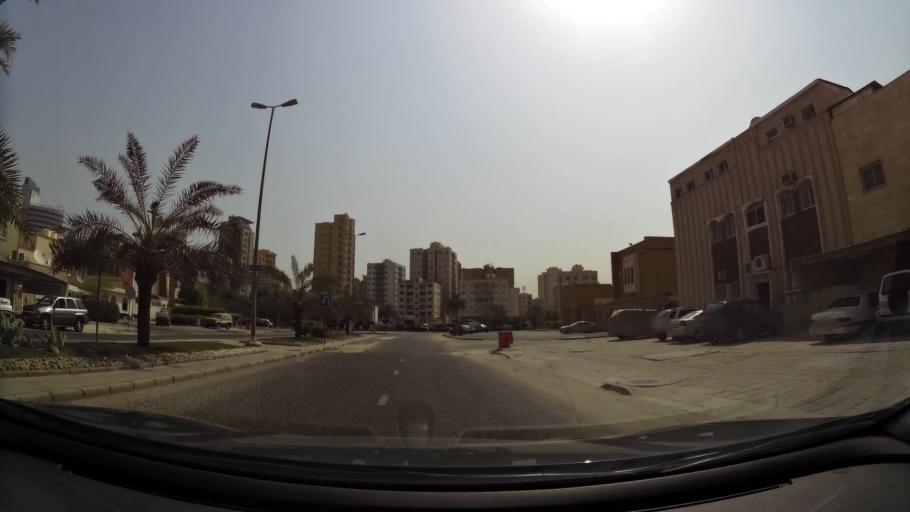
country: KW
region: Al Asimah
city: Ad Dasmah
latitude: 29.3466
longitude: 48.0079
